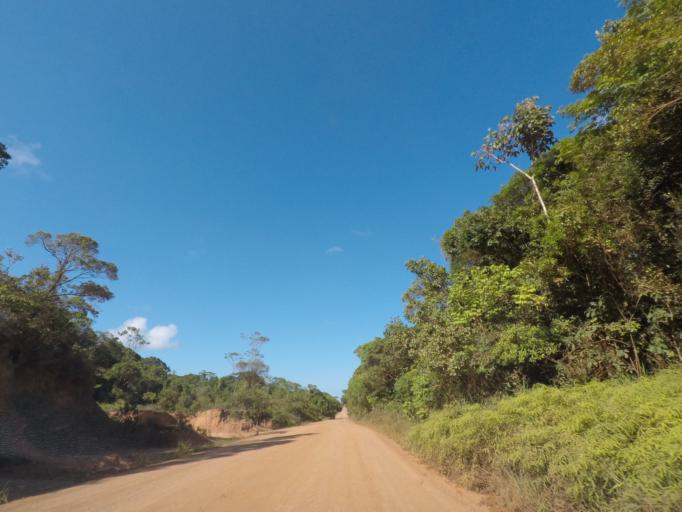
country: BR
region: Bahia
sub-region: Marau
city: Marau
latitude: -14.1207
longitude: -38.9891
